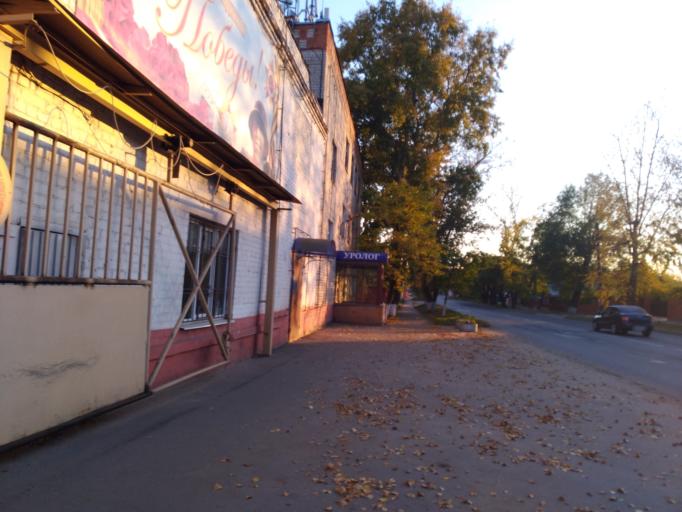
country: RU
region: Kaluga
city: Kaluga
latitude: 54.5211
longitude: 36.2828
